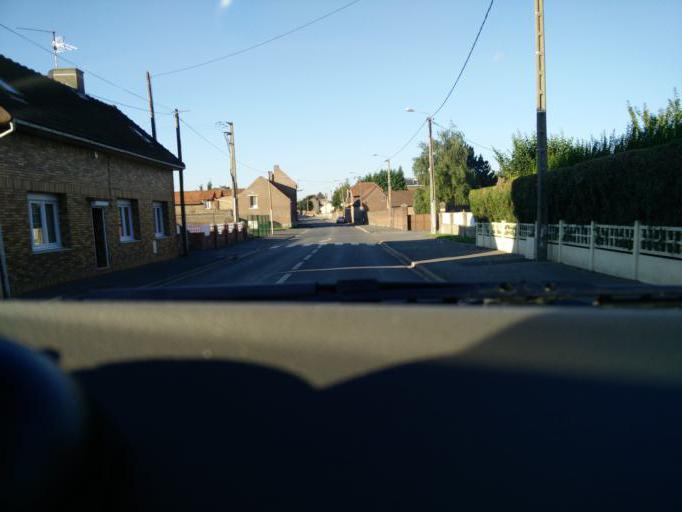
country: FR
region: Nord-Pas-de-Calais
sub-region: Departement du Pas-de-Calais
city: Vermelles
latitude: 50.4878
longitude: 2.7424
